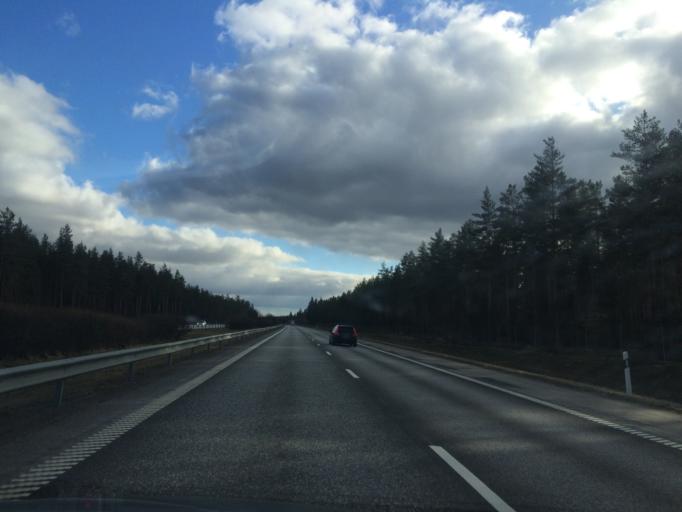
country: SE
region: Joenkoeping
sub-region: Vaggeryds Kommun
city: Skillingaryd
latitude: 57.3895
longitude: 14.0995
